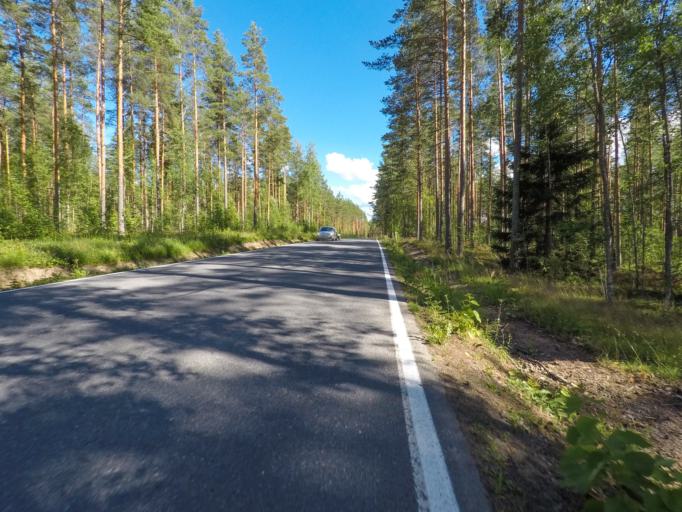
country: FI
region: South Karelia
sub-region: Lappeenranta
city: Taipalsaari
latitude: 61.1777
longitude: 28.0102
